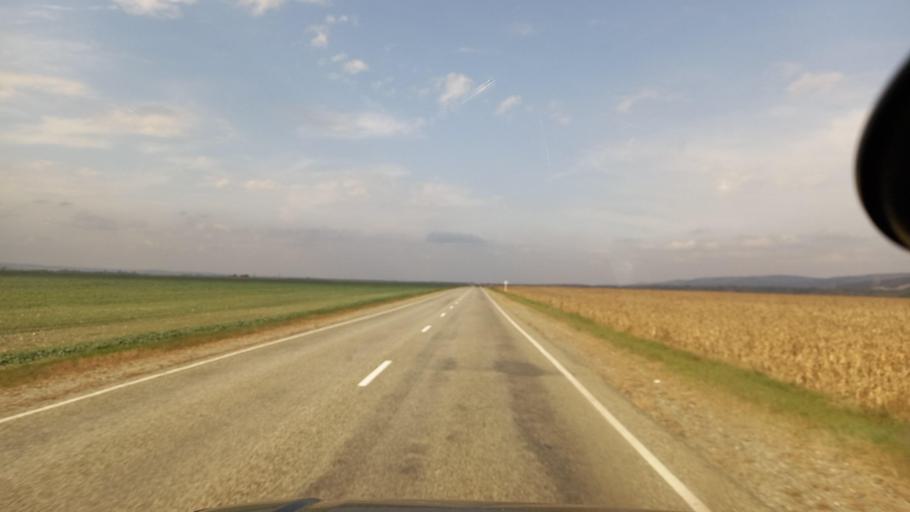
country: RU
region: Krasnodarskiy
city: Perepravnaya
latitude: 44.3063
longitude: 40.8590
